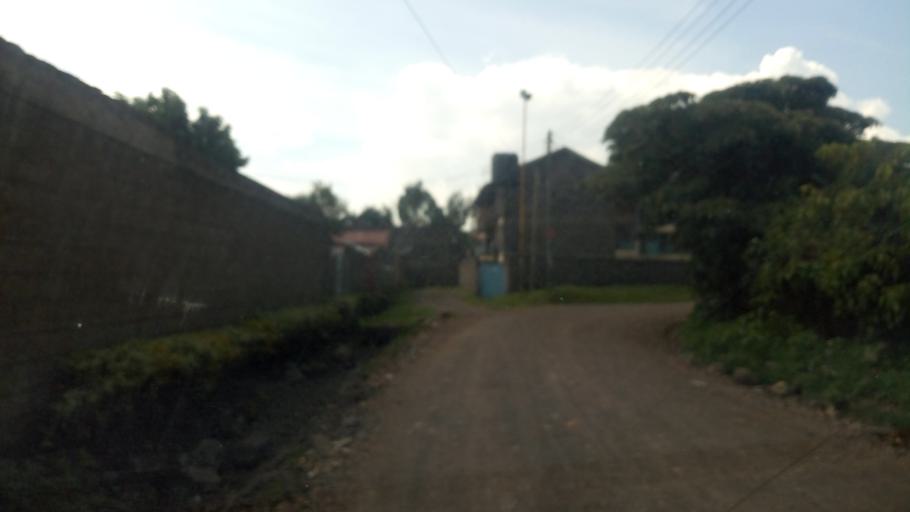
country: KE
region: Nakuru
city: Nakuru
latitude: -0.2774
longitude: 36.1043
